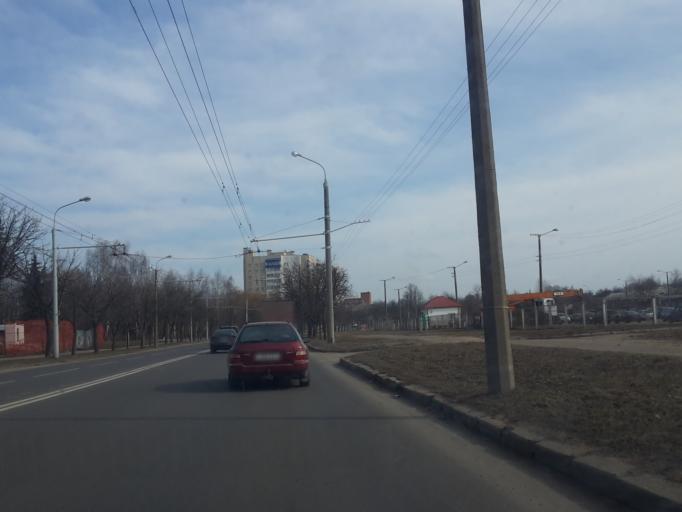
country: BY
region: Minsk
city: Minsk
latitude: 53.8983
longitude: 27.5078
